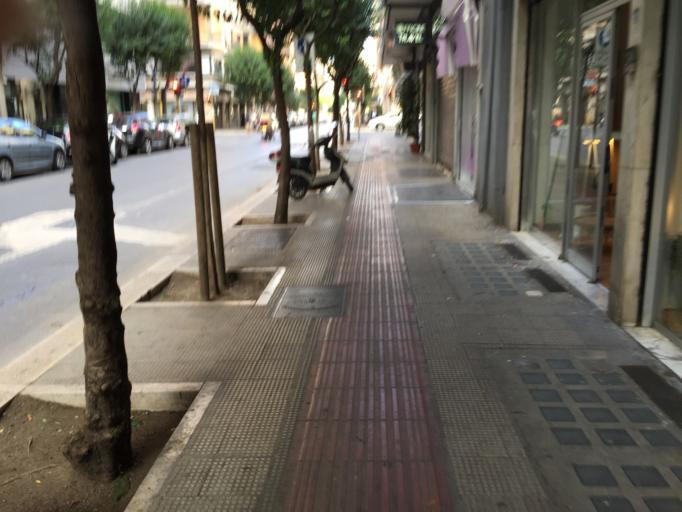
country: IT
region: Apulia
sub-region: Provincia di Bari
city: Bari
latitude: 41.1246
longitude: 16.8652
